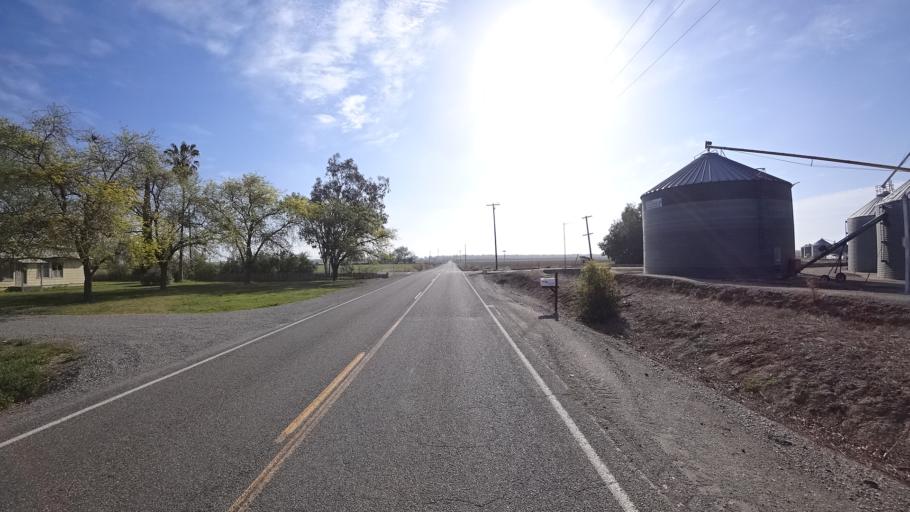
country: US
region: California
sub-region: Glenn County
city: Hamilton City
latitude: 39.5825
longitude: -122.0283
